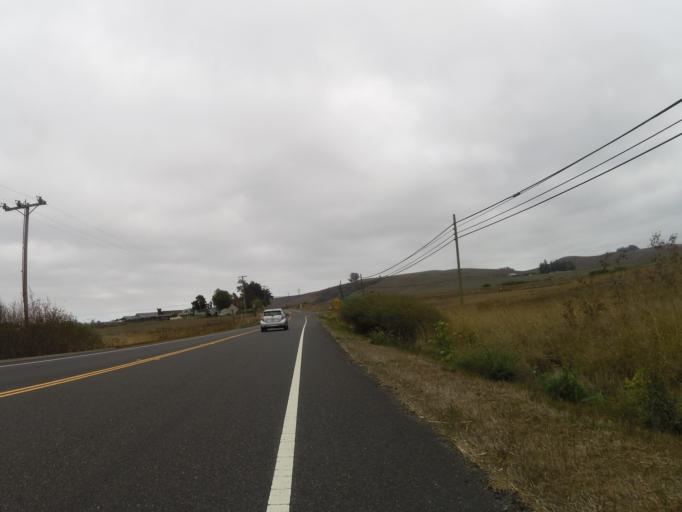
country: US
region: California
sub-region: Sonoma County
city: Occidental
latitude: 38.3174
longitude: -122.8985
